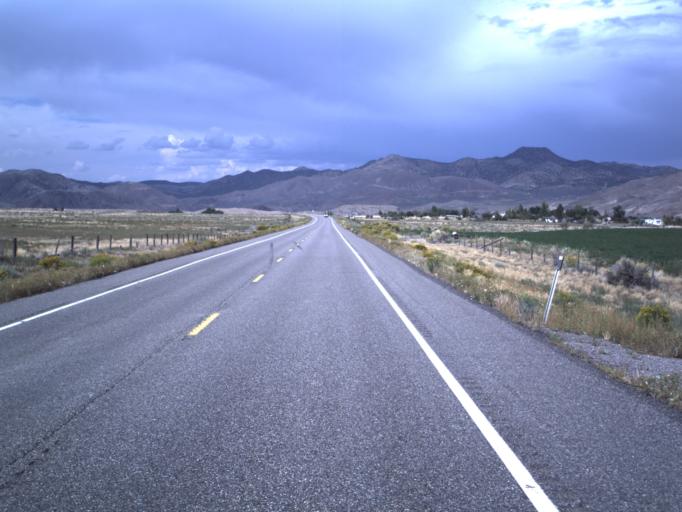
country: US
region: Utah
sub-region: Piute County
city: Junction
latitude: 38.4345
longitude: -112.2309
